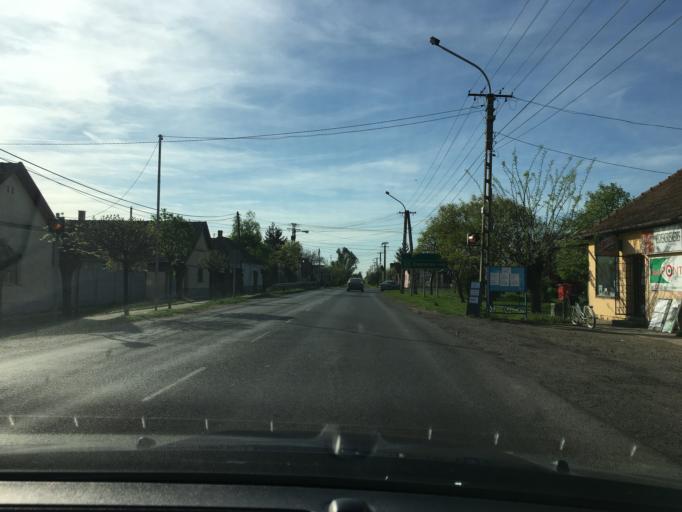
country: HU
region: Bekes
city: Korostarcsa
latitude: 46.8740
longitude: 21.0206
